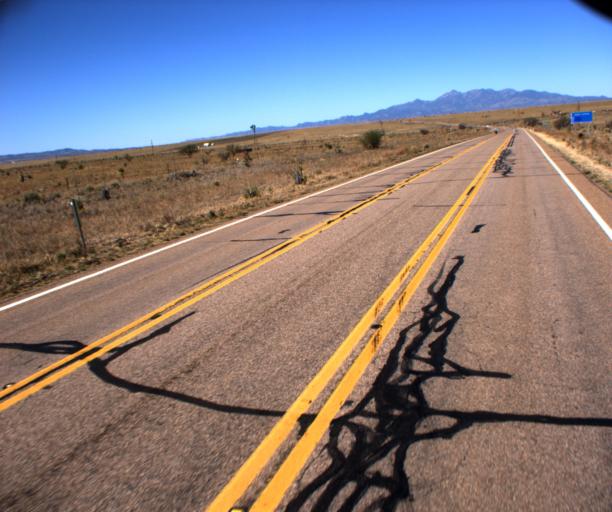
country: US
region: Arizona
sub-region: Cochise County
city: Huachuca City
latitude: 31.7240
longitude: -110.5213
